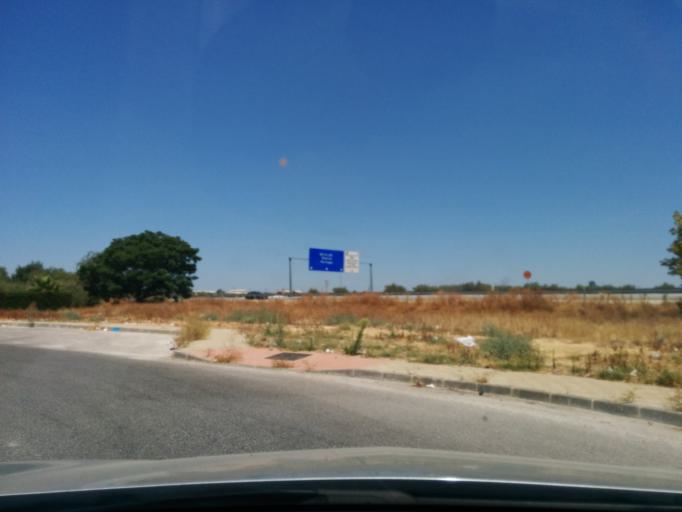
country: ES
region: Andalusia
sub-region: Provincia de Sevilla
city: Benacazon
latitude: 37.3577
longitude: -6.1941
